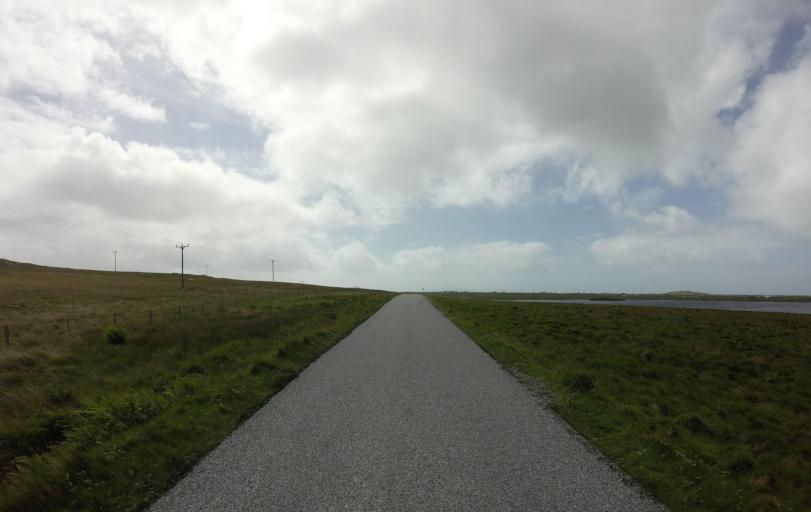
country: GB
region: Scotland
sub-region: Eilean Siar
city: Isle of South Uist
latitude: 57.1457
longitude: -7.3724
